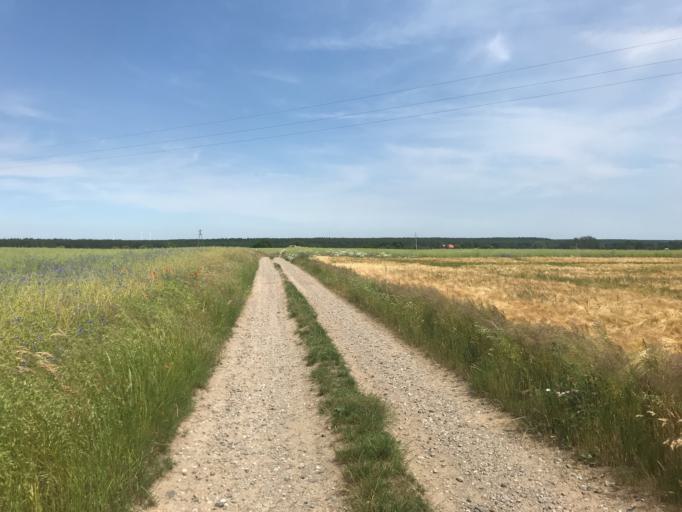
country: PL
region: West Pomeranian Voivodeship
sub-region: Powiat mysliborski
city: Boleszkowice
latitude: 52.6807
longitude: 14.6316
